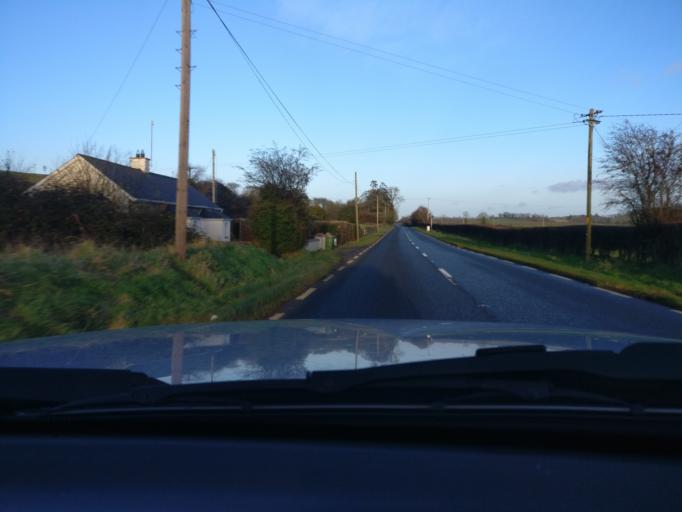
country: IE
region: Leinster
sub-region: Lu
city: Ardee
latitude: 53.8050
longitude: -6.6700
